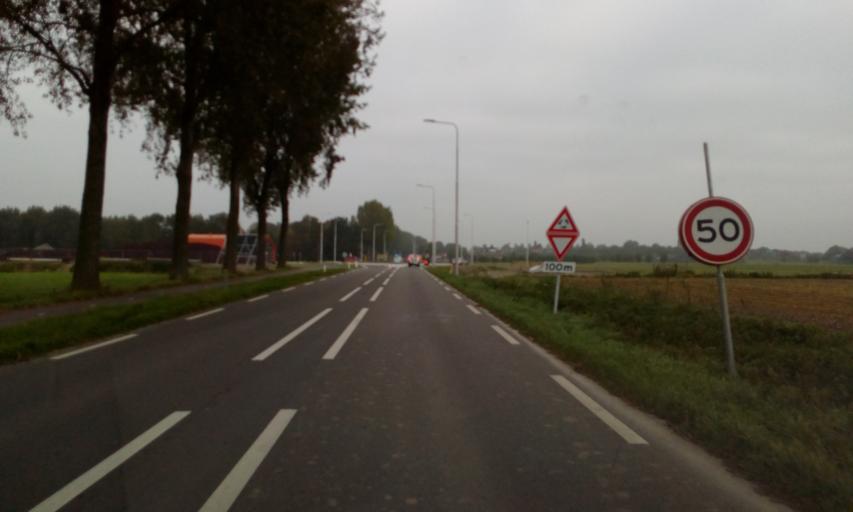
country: NL
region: South Holland
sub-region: Gemeente Rijnwoude
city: Benthuizen
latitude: 52.0894
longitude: 4.5898
